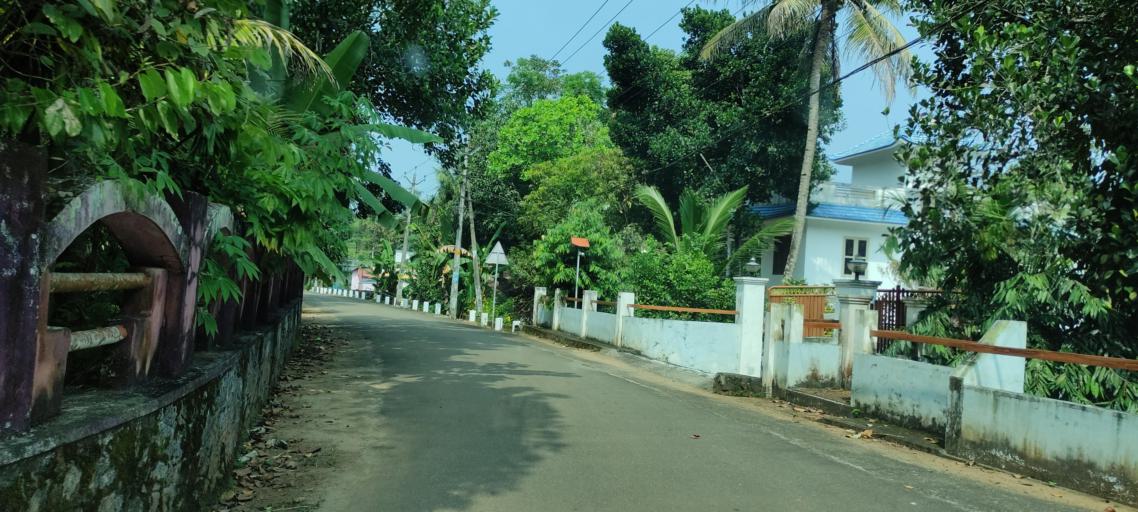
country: IN
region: Kerala
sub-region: Pattanamtitta
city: Adur
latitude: 9.2070
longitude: 76.6927
